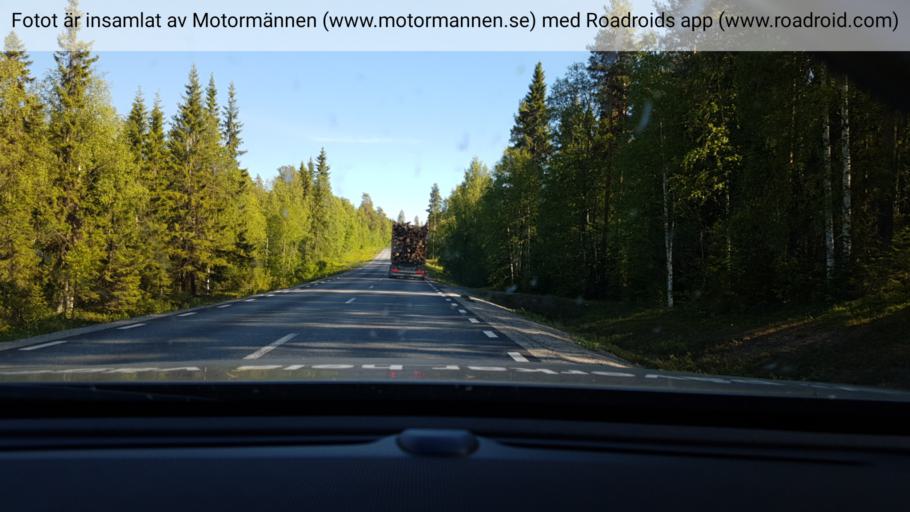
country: SE
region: Vaesterbotten
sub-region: Bjurholms Kommun
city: Bjurholm
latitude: 64.3312
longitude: 19.1491
